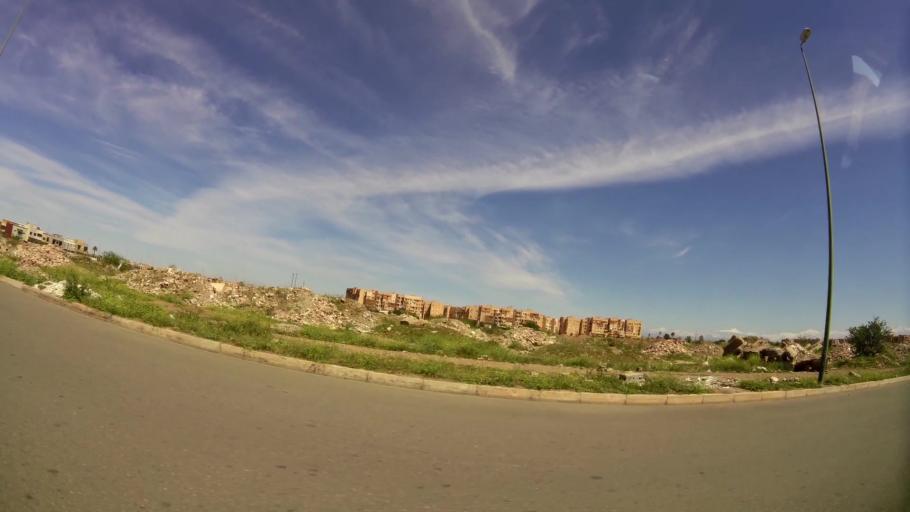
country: MA
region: Marrakech-Tensift-Al Haouz
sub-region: Marrakech
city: Marrakesh
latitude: 31.6482
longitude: -8.0791
